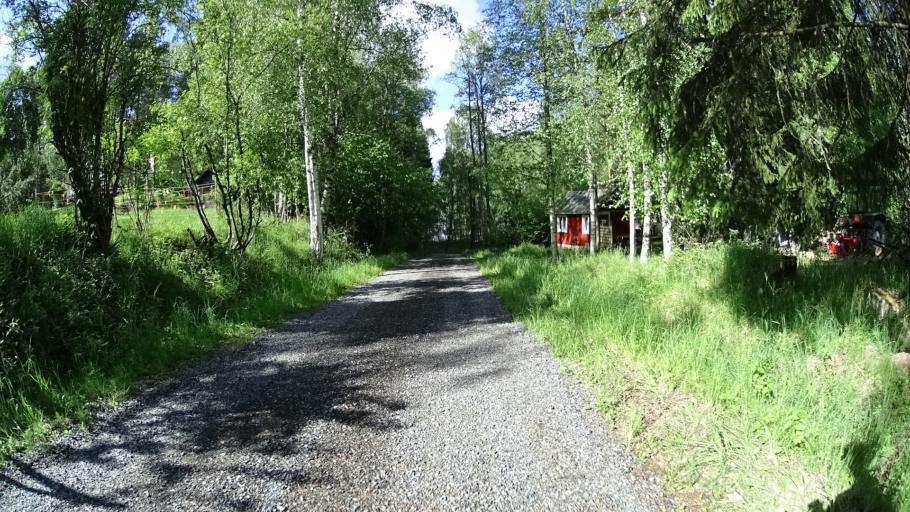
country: FI
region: Varsinais-Suomi
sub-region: Salo
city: Kisko
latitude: 60.1973
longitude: 23.5480
